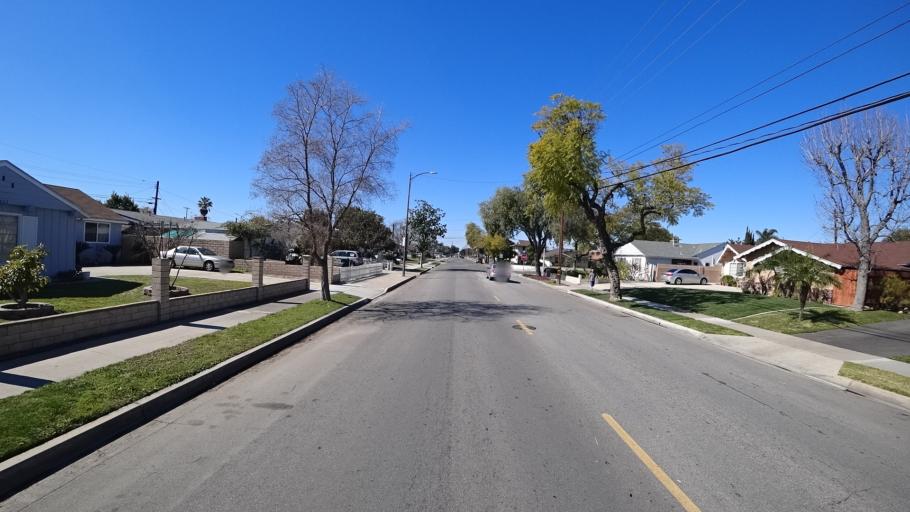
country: US
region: California
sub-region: Orange County
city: Anaheim
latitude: 33.8251
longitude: -117.9491
